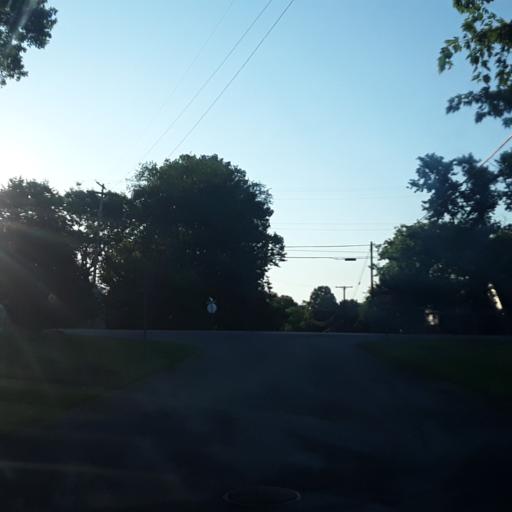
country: US
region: Tennessee
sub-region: Davidson County
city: Oak Hill
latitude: 36.1049
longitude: -86.7295
